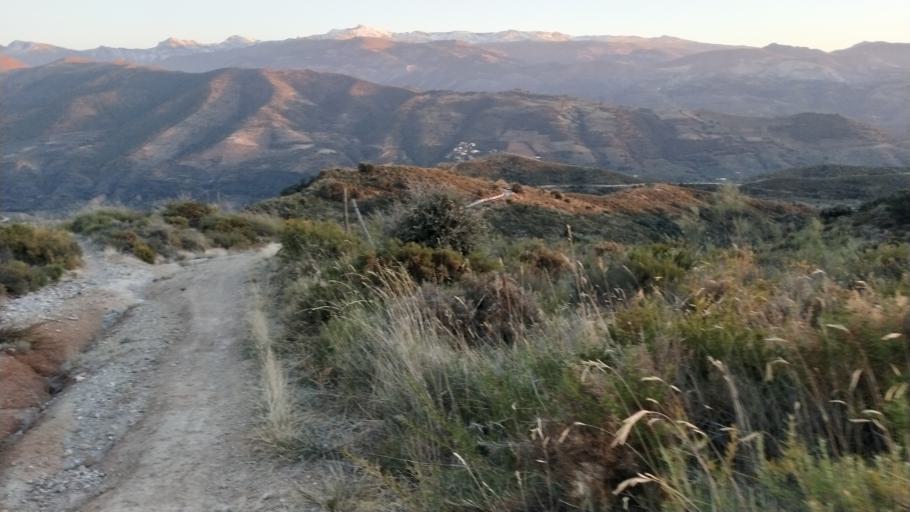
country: ES
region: Andalusia
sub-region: Provincia de Granada
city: Dudar
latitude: 37.1970
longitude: -3.5025
